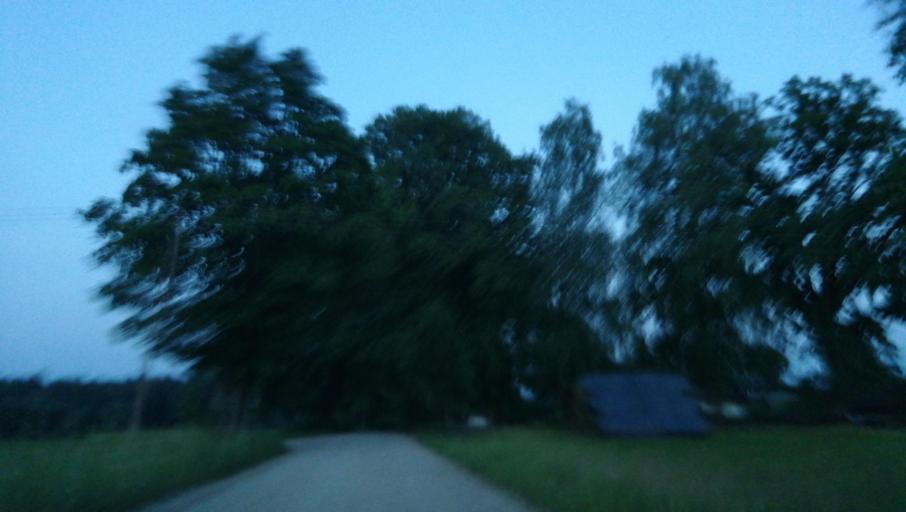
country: LV
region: Ligatne
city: Ligatne
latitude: 57.2594
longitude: 25.1580
